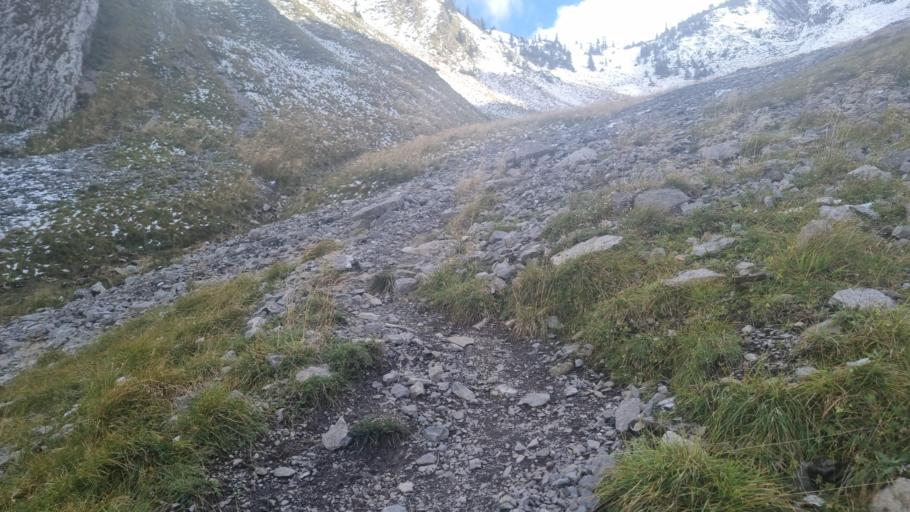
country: CH
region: Schwyz
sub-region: Bezirk March
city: Vorderthal
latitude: 47.0983
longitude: 8.9533
